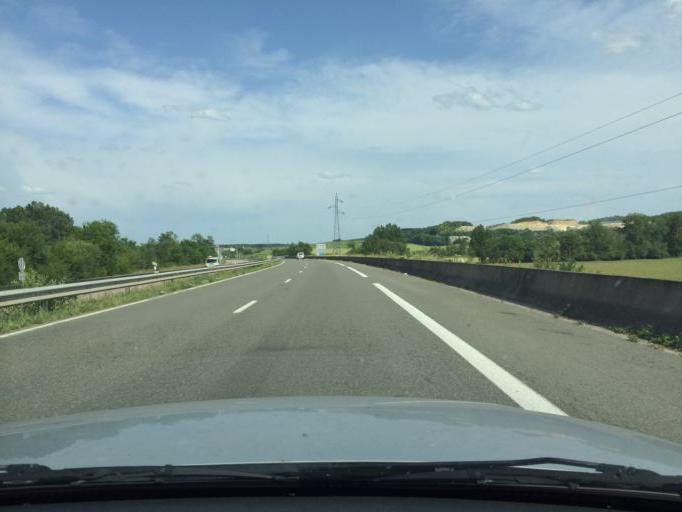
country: FR
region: Lorraine
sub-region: Departement de Meurthe-et-Moselle
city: Foug
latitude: 48.6849
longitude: 5.7144
